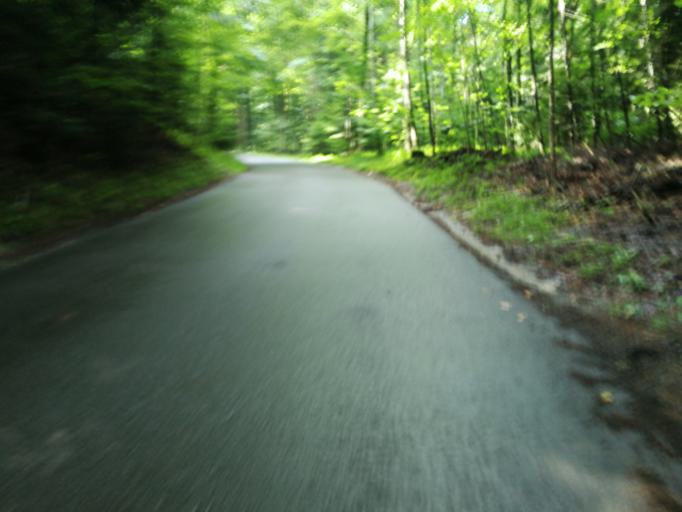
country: CH
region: Schwyz
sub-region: Bezirk Hoefe
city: Feusisberg
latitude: 47.1817
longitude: 8.7761
